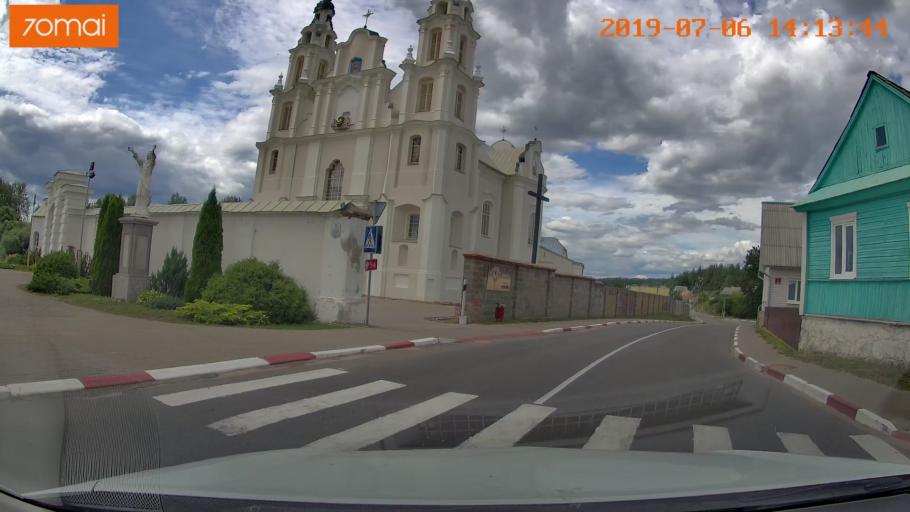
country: BY
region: Minsk
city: Ivyanyets
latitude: 53.8908
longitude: 26.7380
